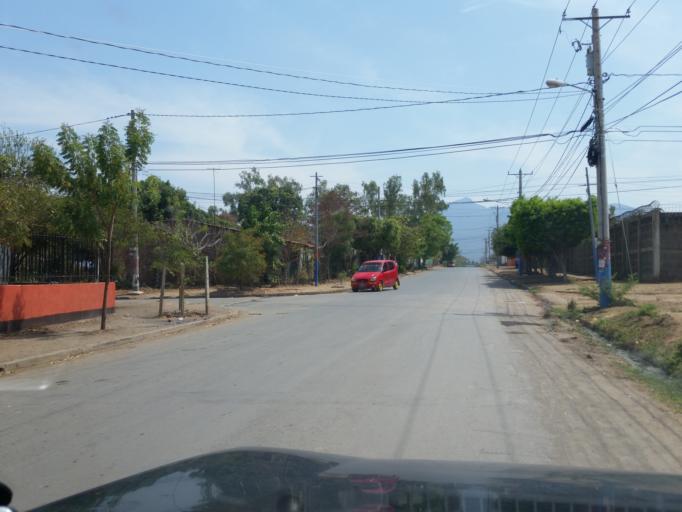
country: NI
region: Granada
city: Granada
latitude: 11.9415
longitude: -85.9621
